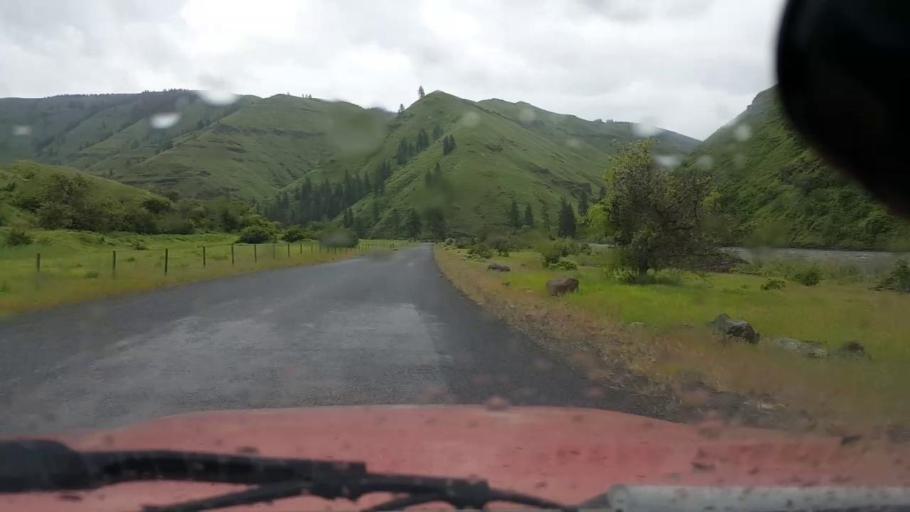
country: US
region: Washington
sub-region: Asotin County
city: Asotin
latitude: 46.0323
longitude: -117.3184
